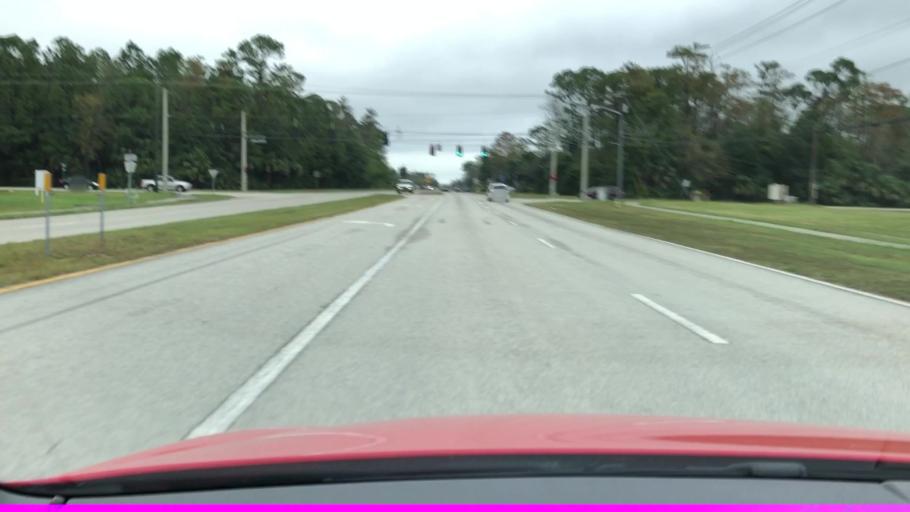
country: US
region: Florida
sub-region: Volusia County
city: Holly Hill
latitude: 29.2102
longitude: -81.0699
